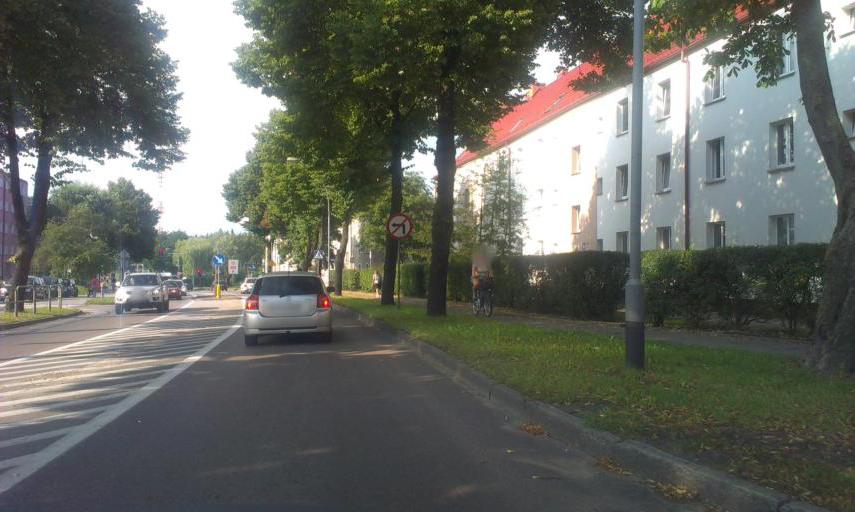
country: PL
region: West Pomeranian Voivodeship
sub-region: Powiat szczecinecki
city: Szczecinek
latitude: 53.7050
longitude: 16.7100
